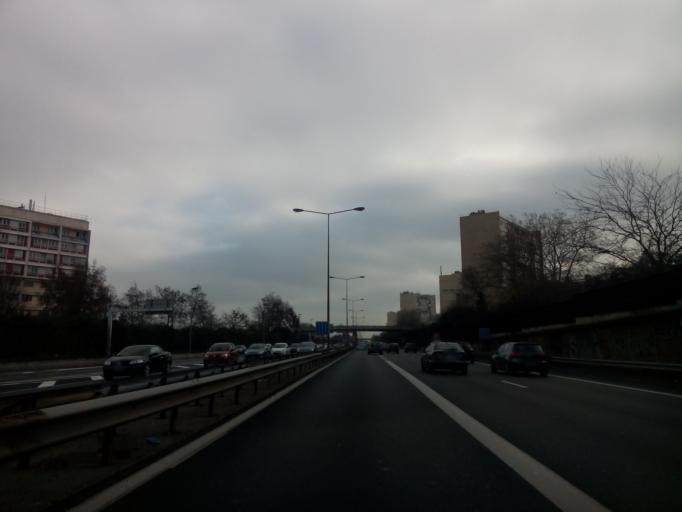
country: FR
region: Rhone-Alpes
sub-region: Departement du Rhone
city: Bron
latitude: 45.7283
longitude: 4.9028
